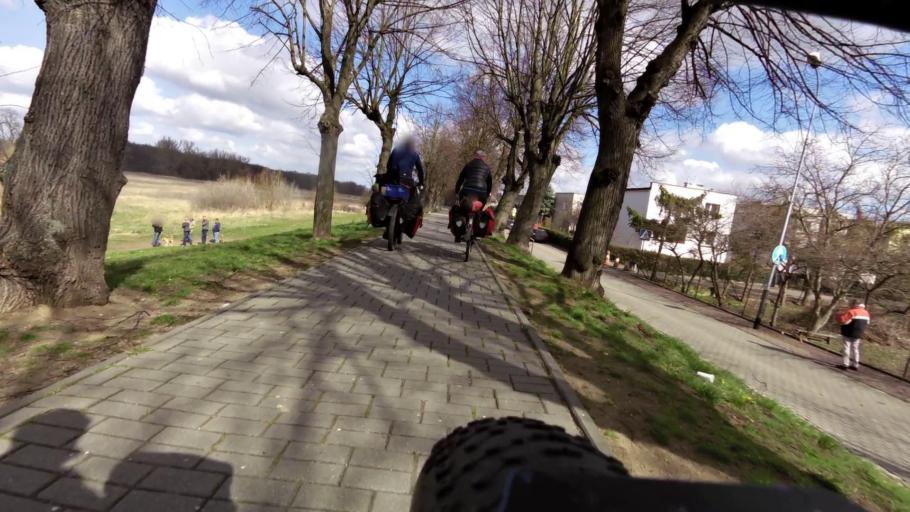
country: PL
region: Lubusz
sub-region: Powiat slubicki
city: Slubice
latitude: 52.3552
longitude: 14.5565
